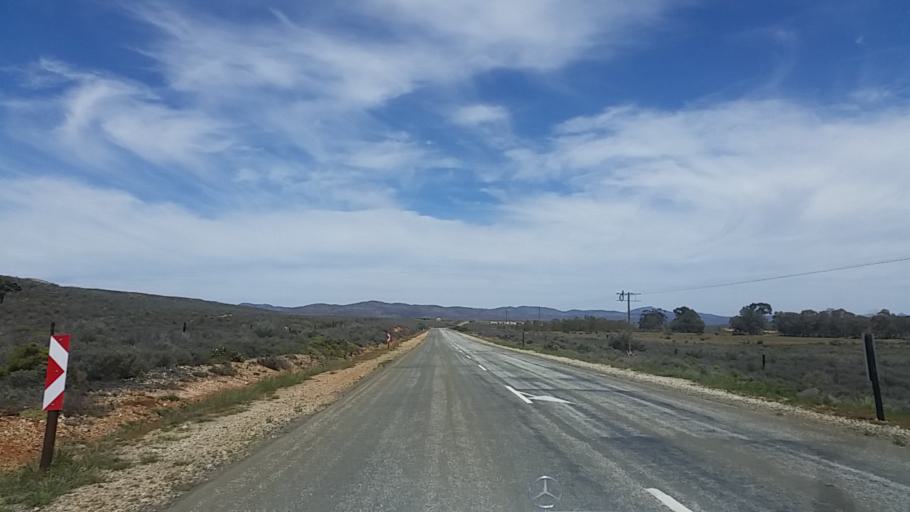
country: ZA
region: Western Cape
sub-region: Eden District Municipality
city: Knysna
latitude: -33.5961
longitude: 23.1509
